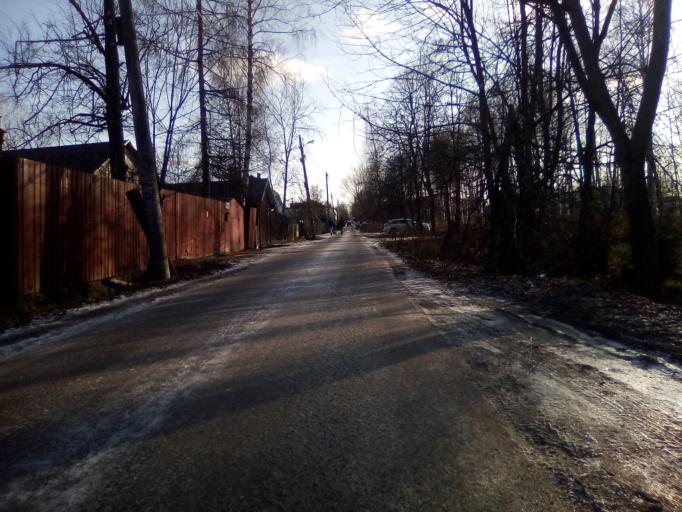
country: RU
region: Moskovskaya
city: Lesnoy Gorodok
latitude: 55.6655
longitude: 37.1804
